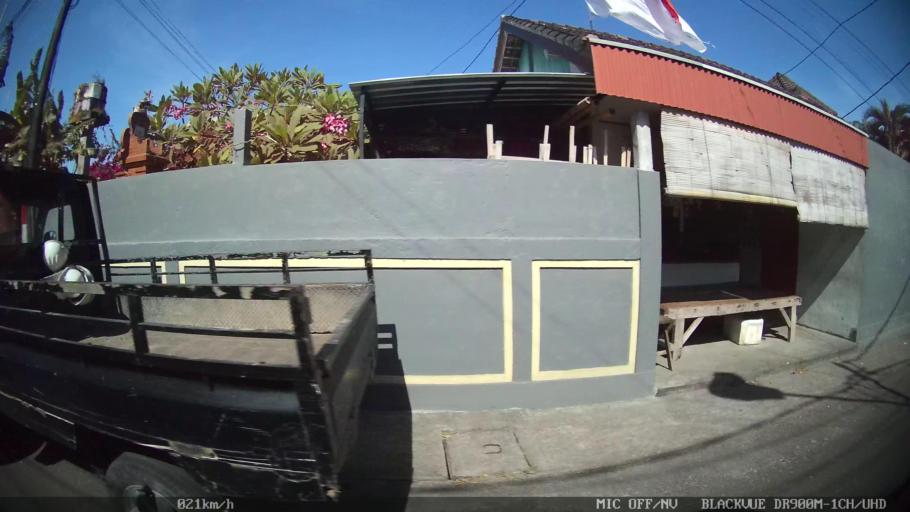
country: ID
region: Bali
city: Denpasar
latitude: -8.6528
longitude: 115.1748
